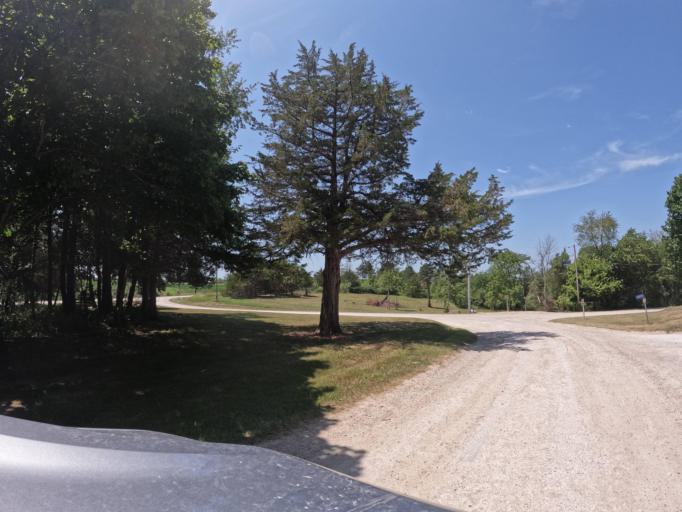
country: US
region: Iowa
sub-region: Henry County
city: Mount Pleasant
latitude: 40.9312
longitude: -91.6178
